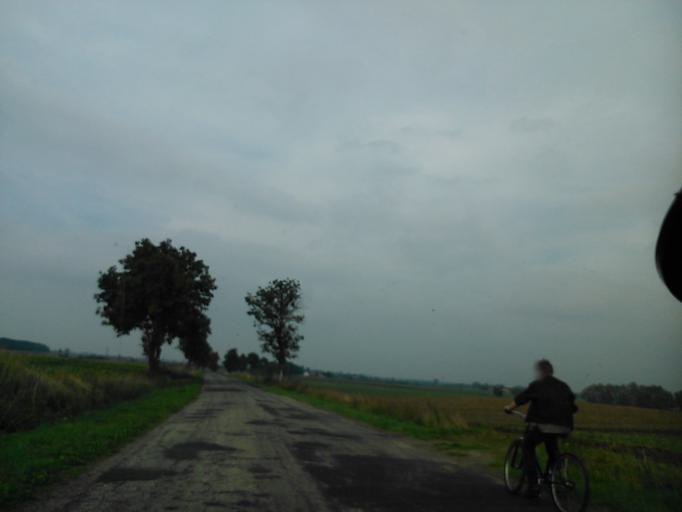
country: PL
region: Kujawsko-Pomorskie
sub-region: Powiat wabrzeski
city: Pluznica
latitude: 53.2410
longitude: 18.8188
